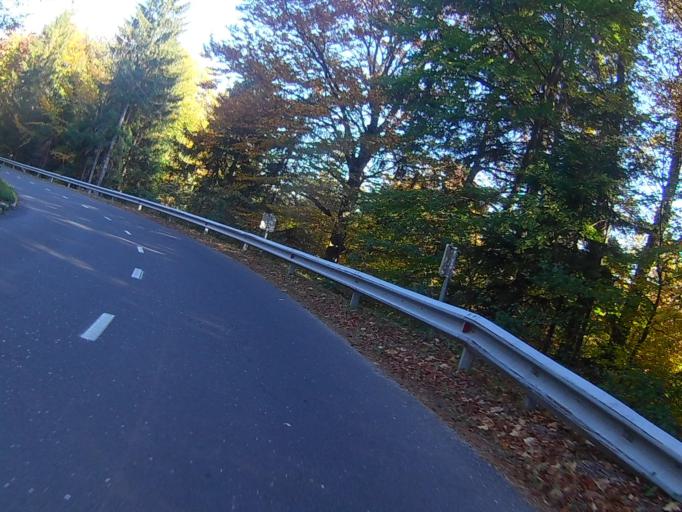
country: SI
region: Race-Fram
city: Fram
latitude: 46.4853
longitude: 15.5827
